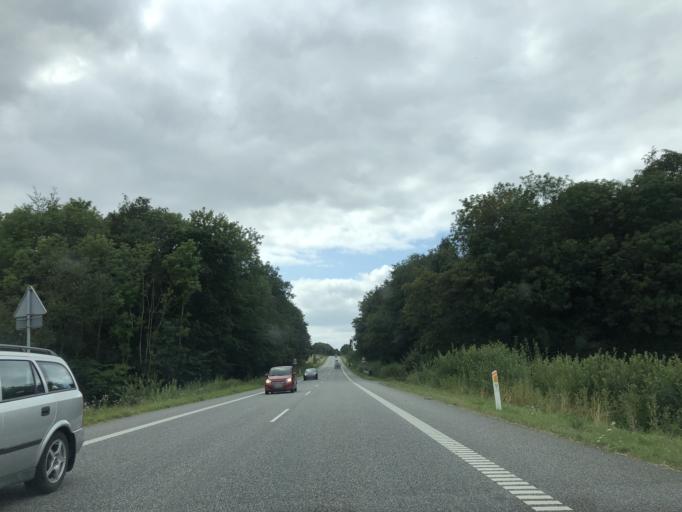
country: DK
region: South Denmark
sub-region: Sonderborg Kommune
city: Guderup
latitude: 54.9824
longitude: 9.9682
